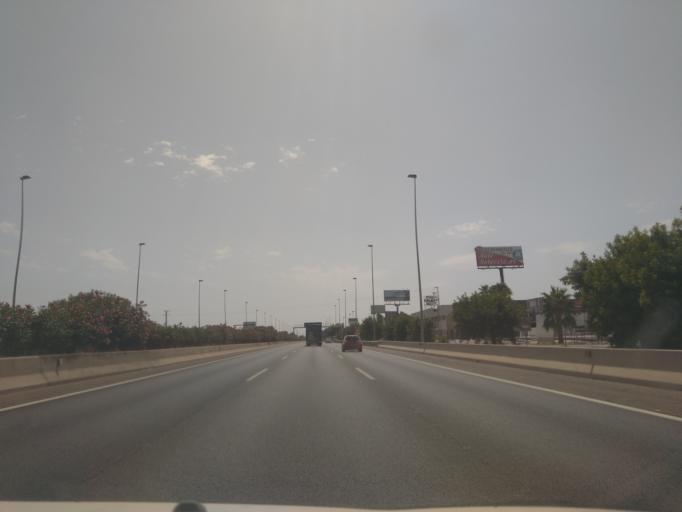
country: ES
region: Valencia
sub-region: Provincia de Valencia
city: Catarroja
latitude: 39.3971
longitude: -0.3894
